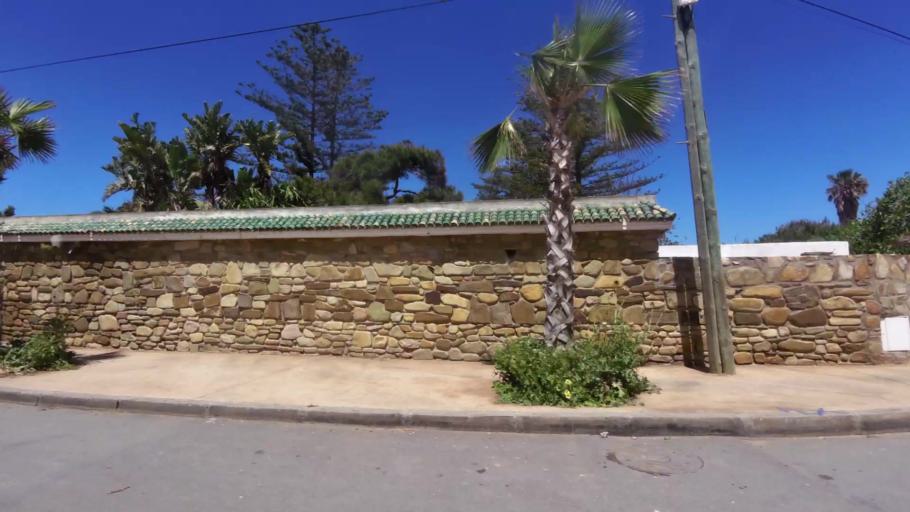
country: MA
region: Grand Casablanca
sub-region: Nouaceur
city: Dar Bouazza
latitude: 33.5264
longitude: -7.8159
